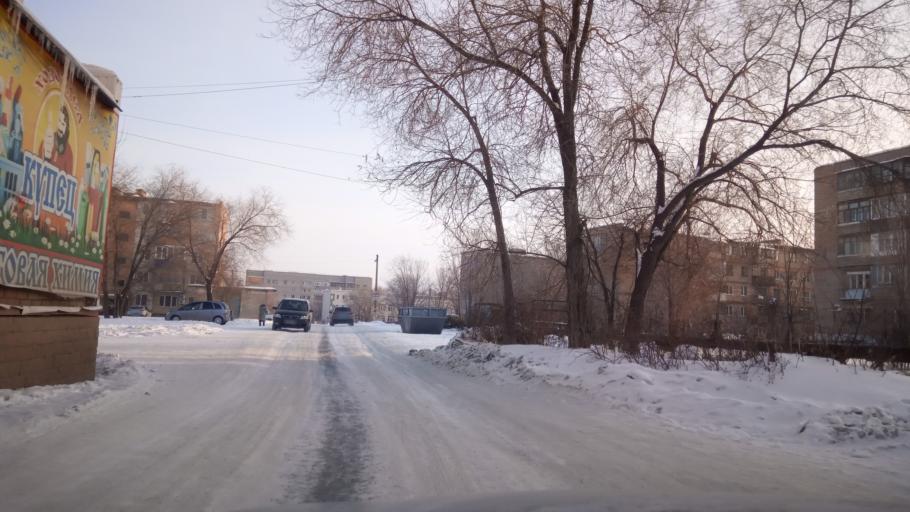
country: RU
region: Orenburg
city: Novotroitsk
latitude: 51.1966
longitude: 58.2846
